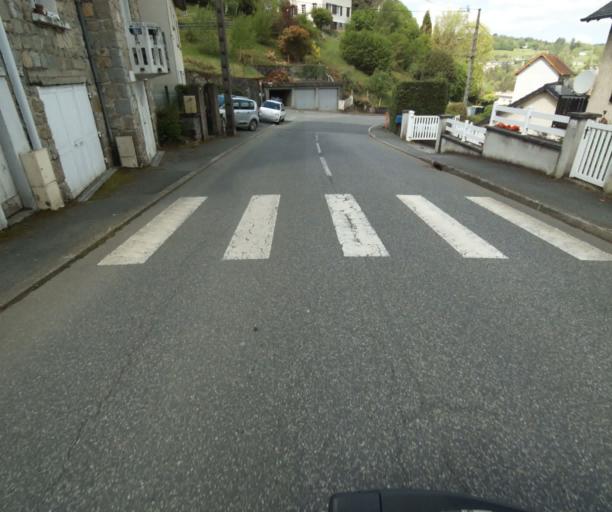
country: FR
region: Limousin
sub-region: Departement de la Correze
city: Tulle
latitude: 45.2684
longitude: 1.7774
